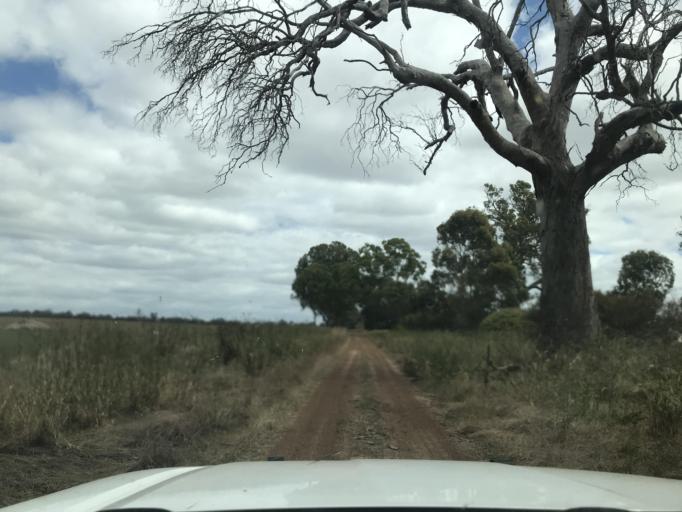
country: AU
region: South Australia
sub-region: Naracoorte and Lucindale
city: Naracoorte
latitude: -36.9832
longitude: 141.3907
